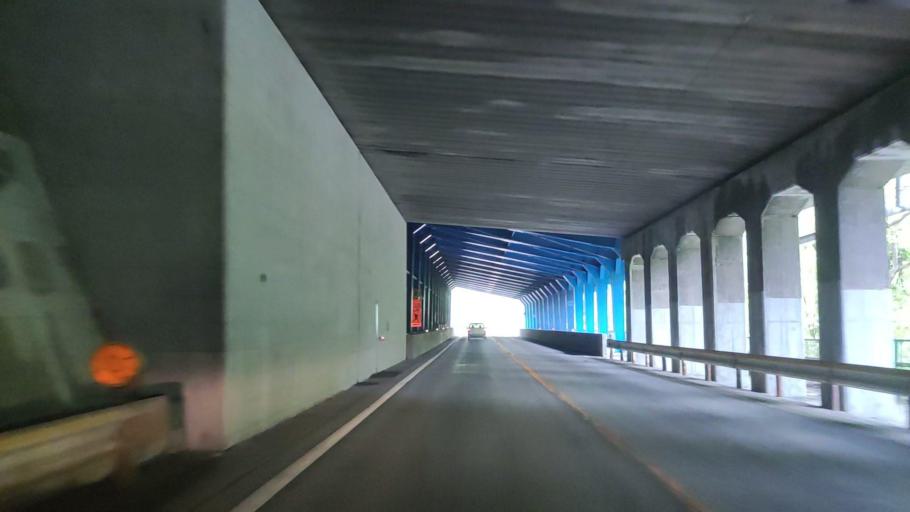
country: JP
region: Gifu
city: Takayama
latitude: 36.3539
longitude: 137.2875
